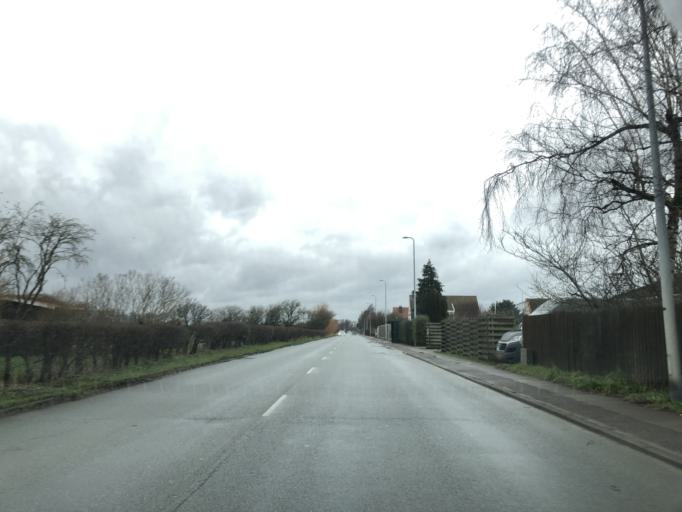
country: DK
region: Capital Region
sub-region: Dragor Kommune
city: Dragor
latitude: 55.5853
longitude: 12.6361
